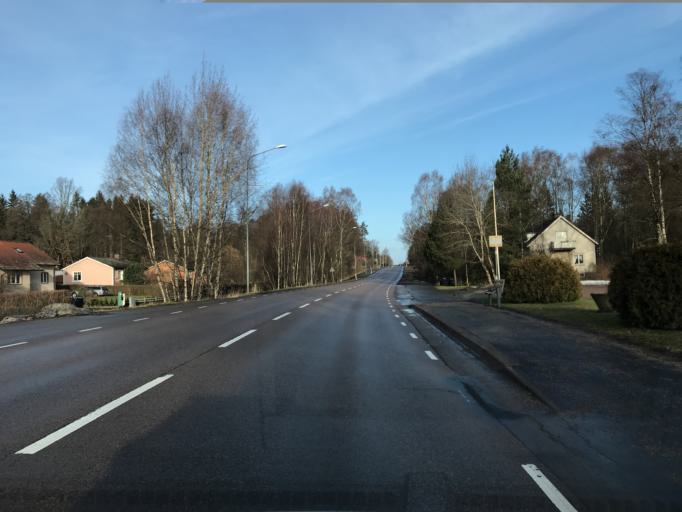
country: SE
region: Skane
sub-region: Hassleholms Kommun
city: Bjarnum
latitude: 56.3029
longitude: 13.6997
